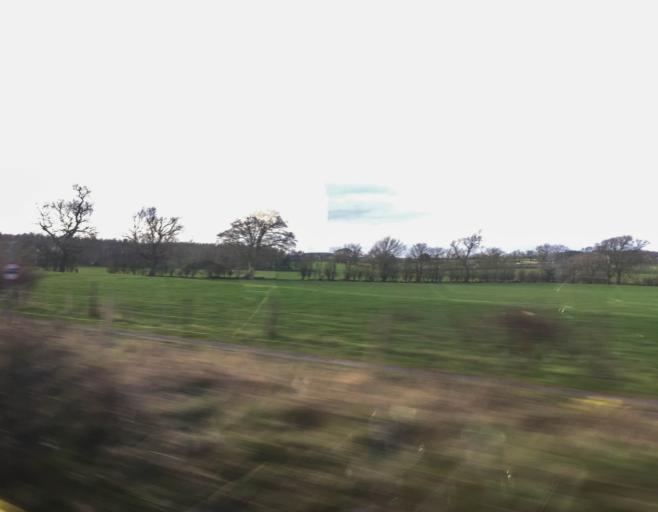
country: GB
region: Scotland
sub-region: Dumfries and Galloway
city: Gretna
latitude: 55.0218
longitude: -3.1163
